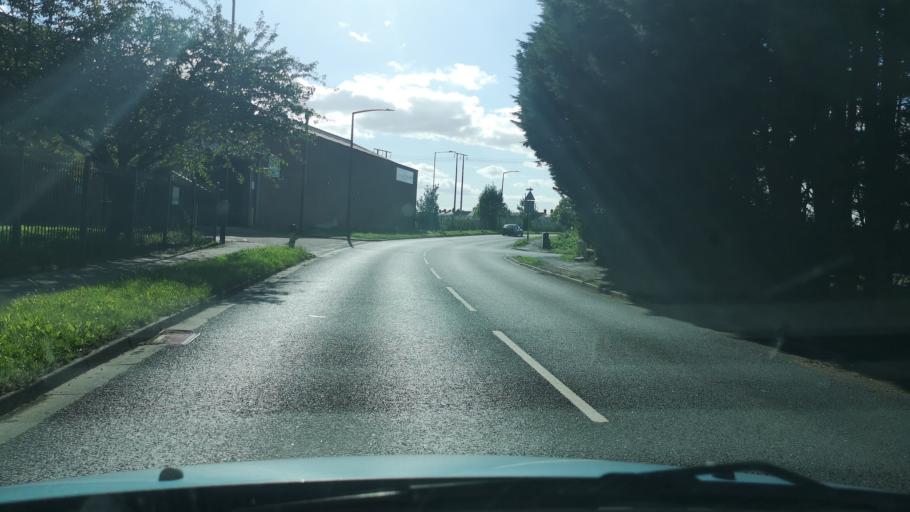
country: GB
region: England
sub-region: Doncaster
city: Bentley
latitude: 53.5507
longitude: -1.1344
